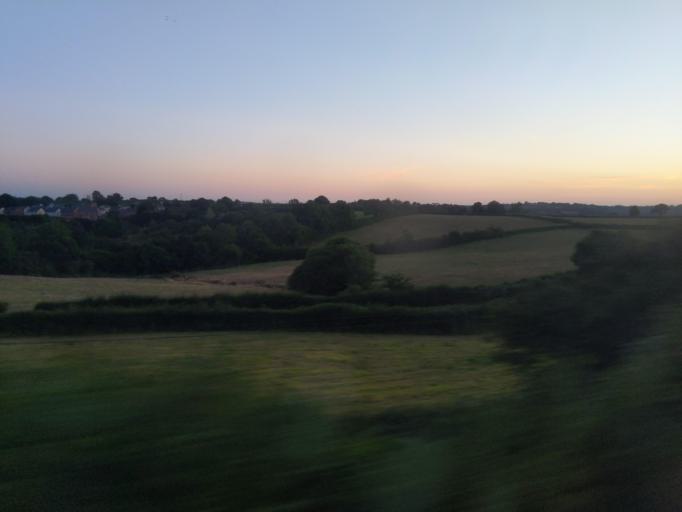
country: GB
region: England
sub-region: Devon
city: Ivybridge
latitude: 50.3969
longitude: -3.9399
